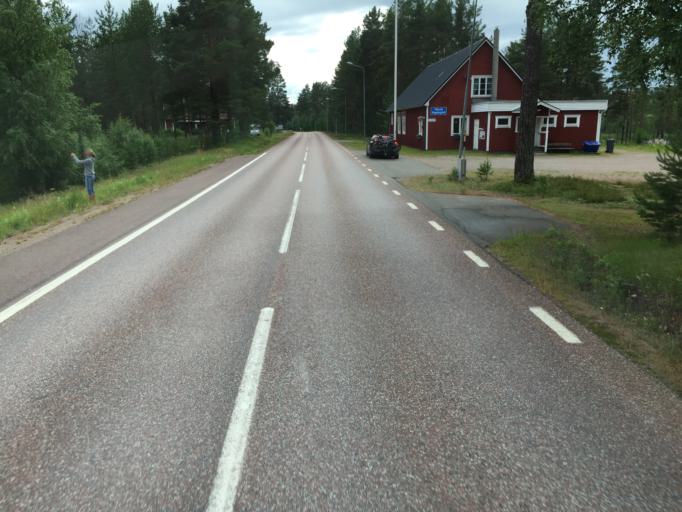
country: SE
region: Dalarna
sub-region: Vansbro Kommun
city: Vansbro
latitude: 60.7791
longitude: 14.1522
